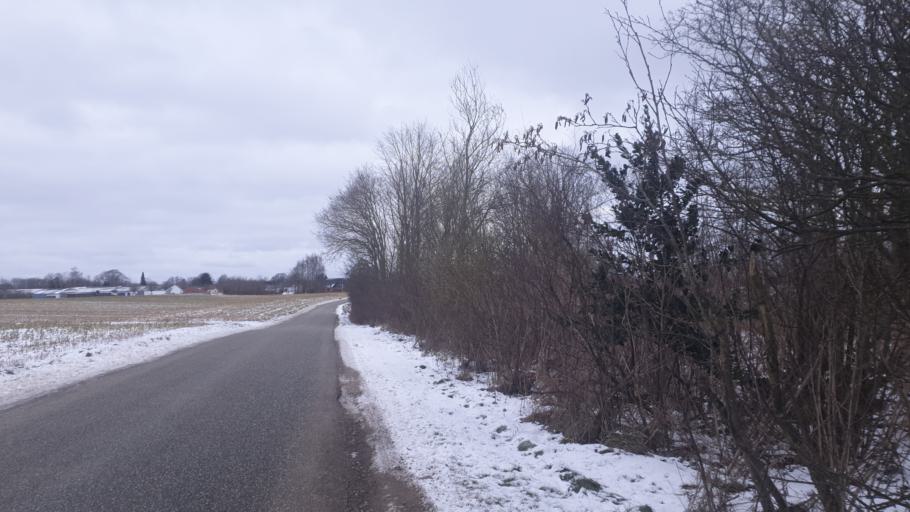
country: DK
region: Central Jutland
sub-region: Hedensted Kommune
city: Hedensted
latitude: 55.7988
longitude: 9.7061
